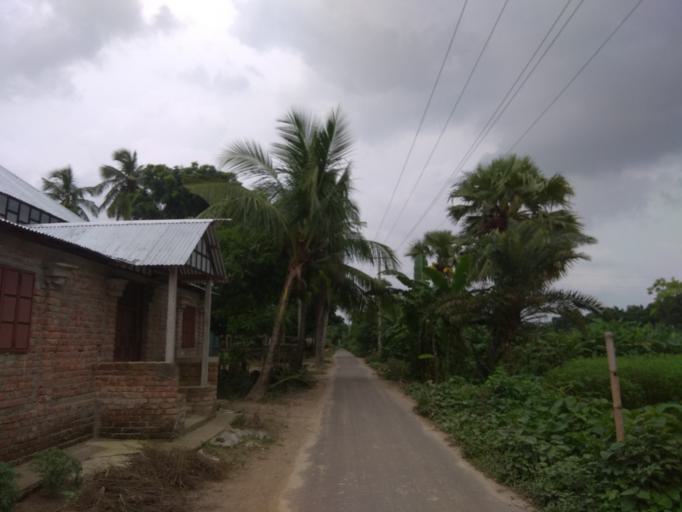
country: BD
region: Dhaka
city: Faridpur
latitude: 23.4897
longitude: 89.9841
